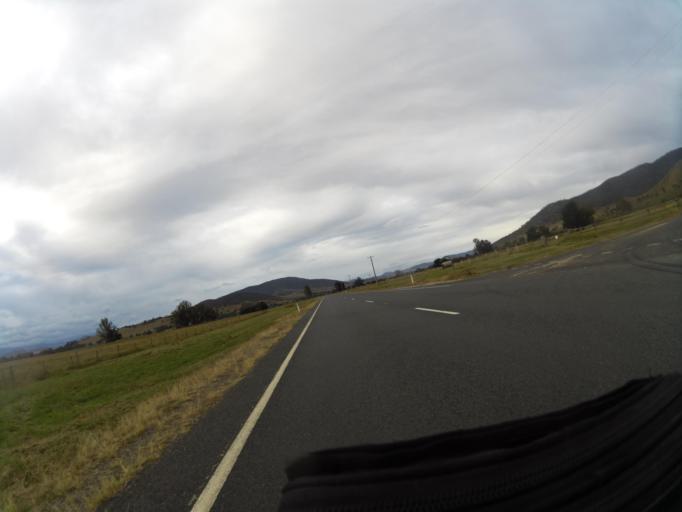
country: AU
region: New South Wales
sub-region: Snowy River
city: Jindabyne
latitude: -36.1092
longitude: 147.9796
